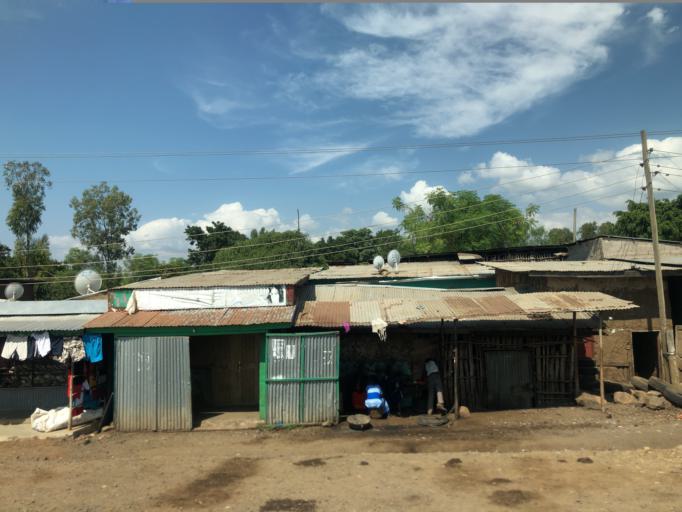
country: ET
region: Southern Nations, Nationalities, and People's Region
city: Arba Minch'
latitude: 5.8656
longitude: 37.4783
